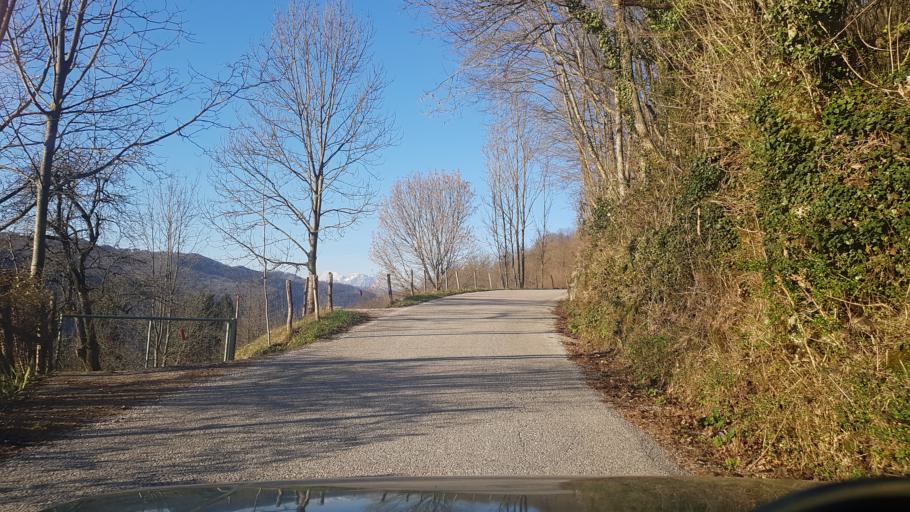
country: SI
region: Kanal
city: Kanal
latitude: 46.0721
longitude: 13.6355
